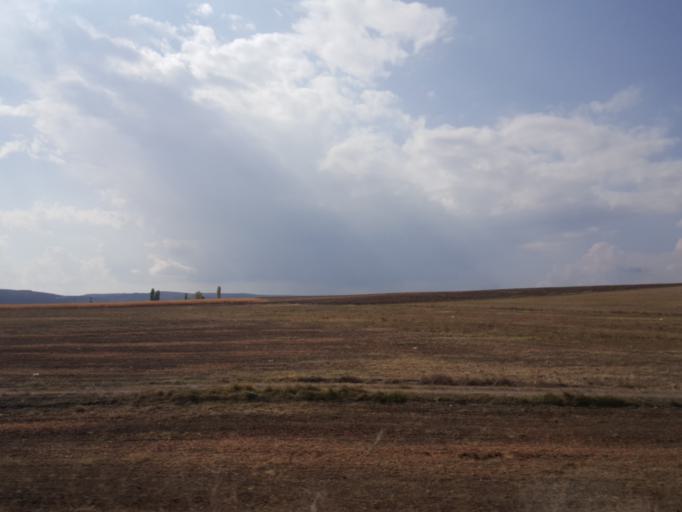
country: TR
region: Corum
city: Alaca
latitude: 40.1480
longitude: 34.8857
